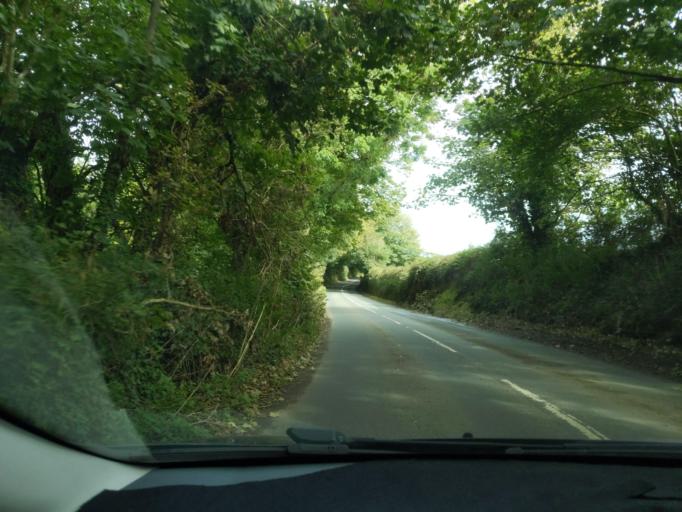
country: GB
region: England
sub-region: Cornwall
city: Mevagissey
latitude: 50.2467
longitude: -4.8136
